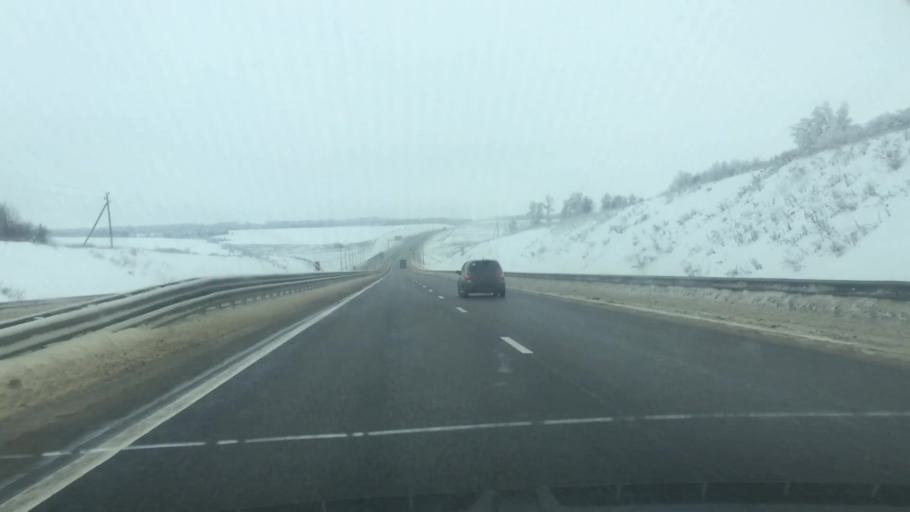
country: RU
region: Lipetsk
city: Stanovoye
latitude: 52.8700
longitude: 38.2815
